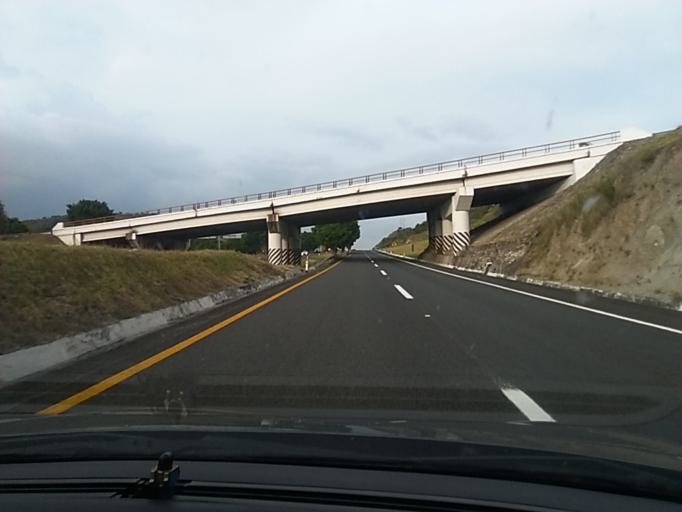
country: MX
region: Michoacan
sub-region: Cuitzeo
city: San Juan Benito Juarez (San Juan Tararameo)
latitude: 19.8970
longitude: -101.1470
